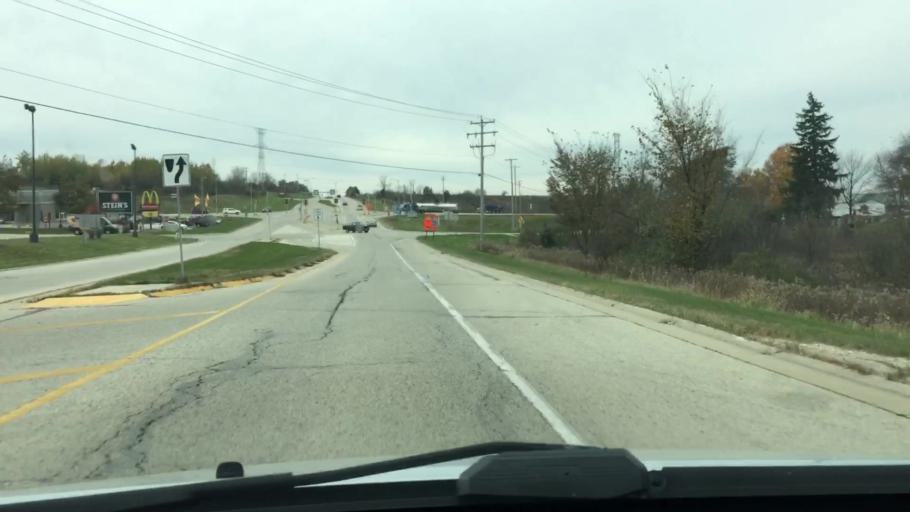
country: US
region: Wisconsin
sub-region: Waukesha County
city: Big Bend
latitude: 42.9147
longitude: -88.2165
